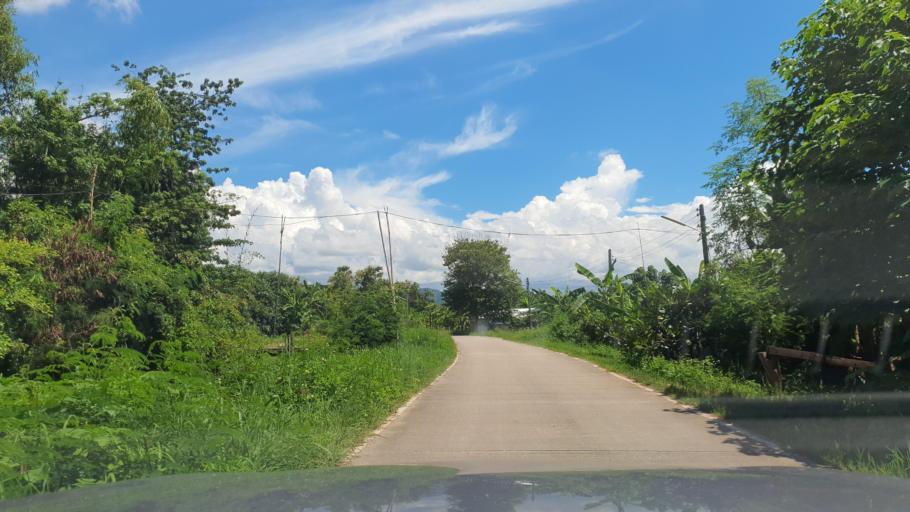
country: TH
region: Chiang Mai
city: San Kamphaeng
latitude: 18.7312
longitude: 99.1216
